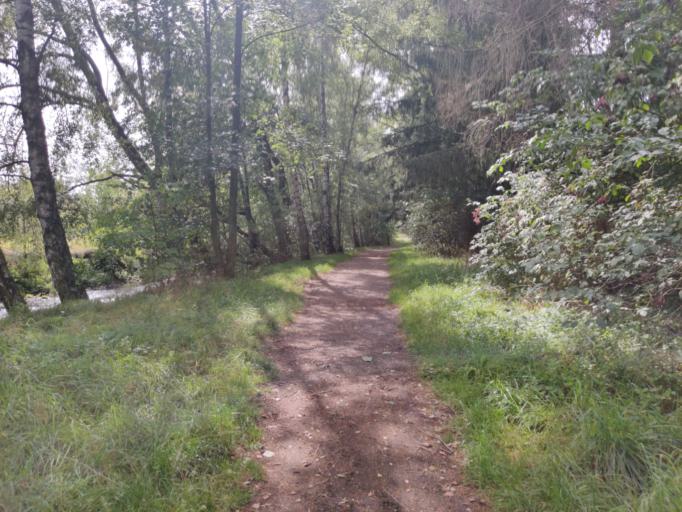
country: DE
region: Lower Saxony
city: Langelsheim
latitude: 51.9436
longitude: 10.3494
